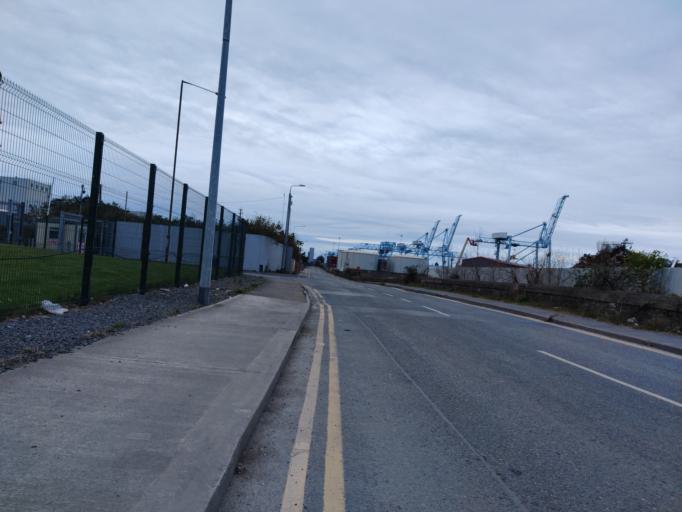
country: IE
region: Leinster
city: Sandymount
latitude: 53.3405
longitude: -6.2000
